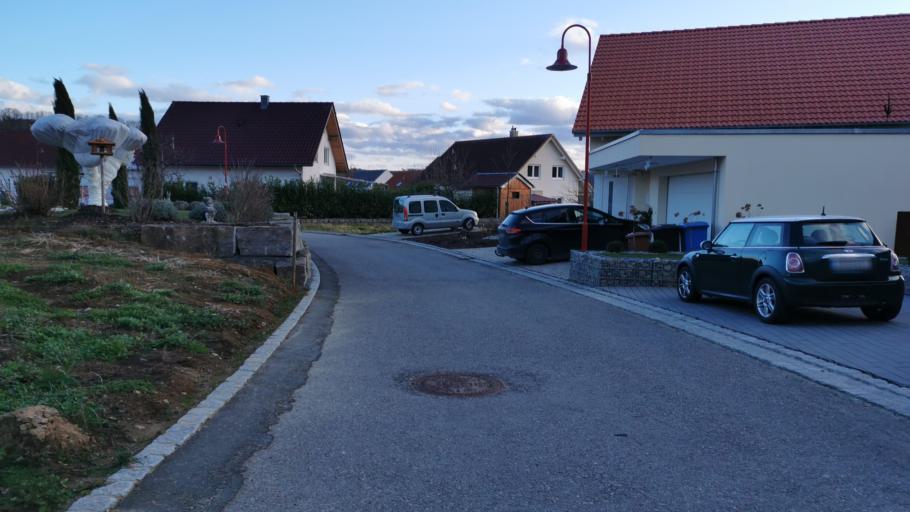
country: DE
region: Baden-Wuerttemberg
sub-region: Regierungsbezirk Stuttgart
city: Jagsthausen
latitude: 49.3140
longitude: 9.4646
